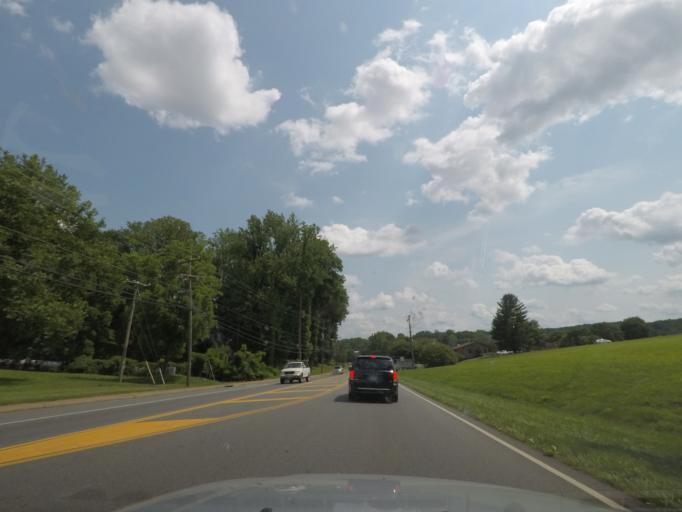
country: US
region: Virginia
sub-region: Orange County
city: Orange
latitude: 38.2555
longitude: -78.1154
